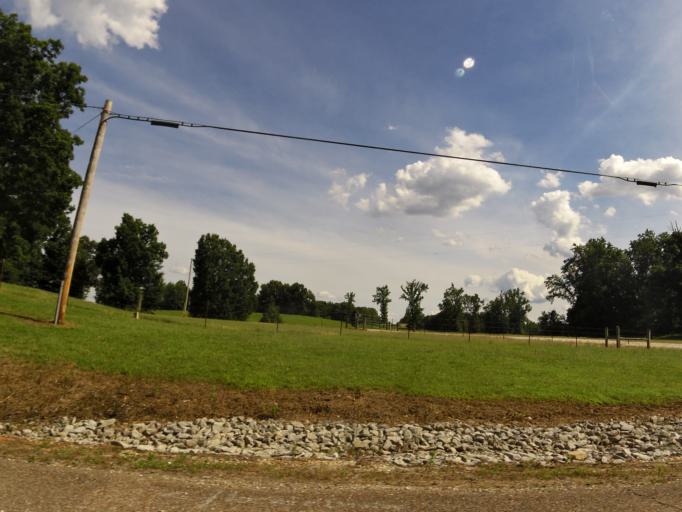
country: US
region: Tennessee
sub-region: Carroll County
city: Huntingdon
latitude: 36.0046
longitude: -88.5425
